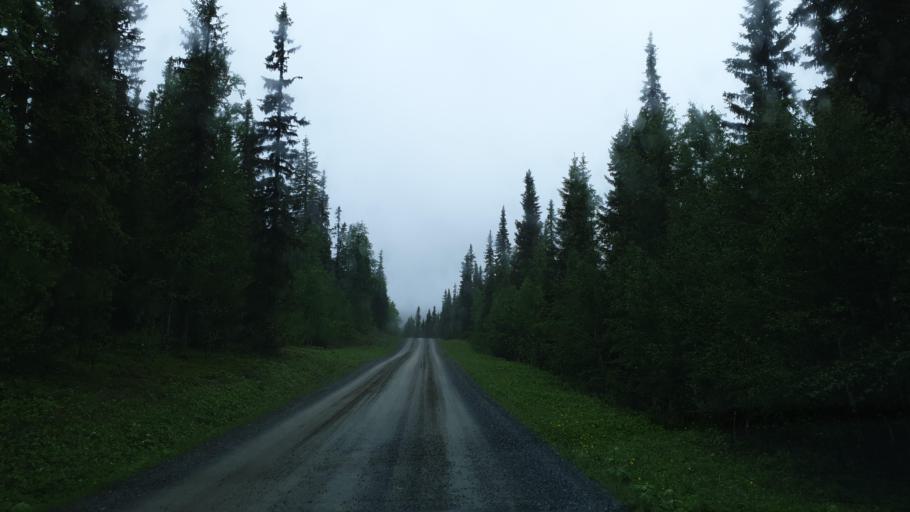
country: SE
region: Vaesterbotten
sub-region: Vilhelmina Kommun
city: Sjoberg
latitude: 65.2745
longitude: 15.9091
